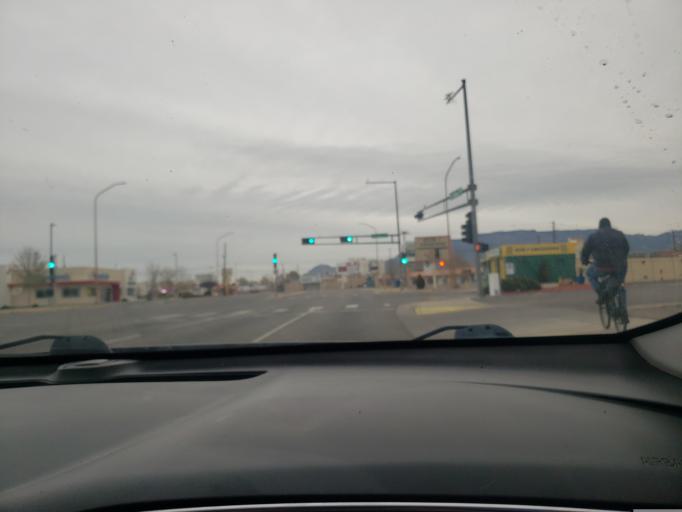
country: US
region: New Mexico
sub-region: Bernalillo County
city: Albuquerque
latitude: 35.1066
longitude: -106.5873
